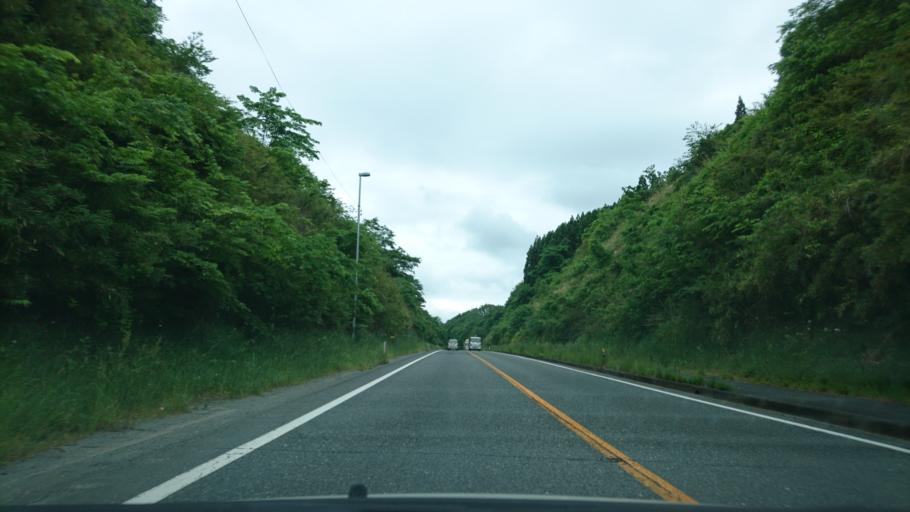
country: JP
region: Iwate
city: Ichinoseki
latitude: 38.8938
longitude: 141.1157
